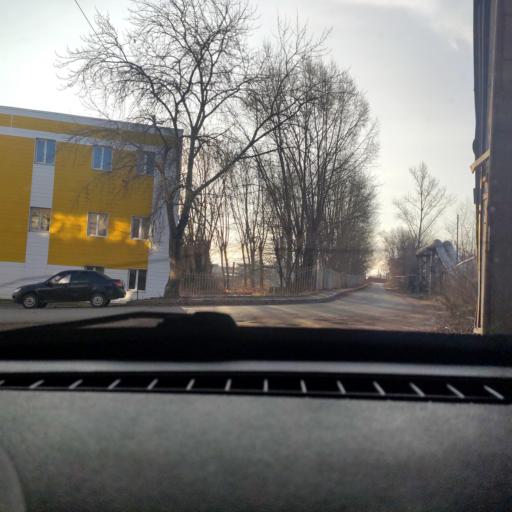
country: RU
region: Bashkortostan
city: Ufa
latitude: 54.8371
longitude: 56.1157
